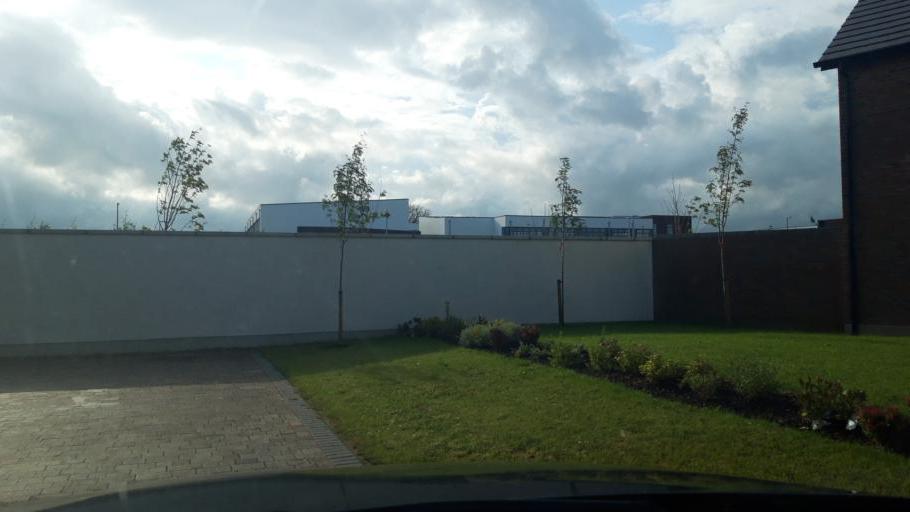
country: IE
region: Leinster
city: Hartstown
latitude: 53.3897
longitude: -6.4439
